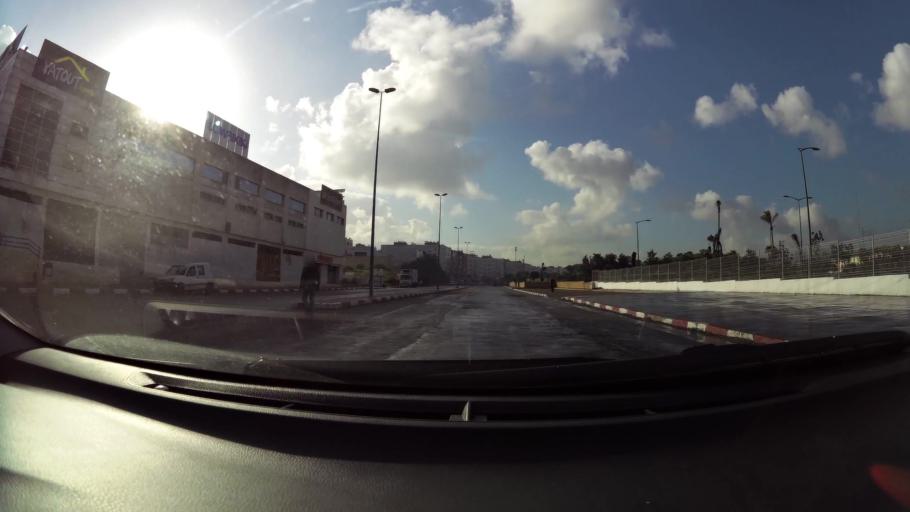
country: MA
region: Grand Casablanca
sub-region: Mediouna
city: Tit Mellil
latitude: 33.6017
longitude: -7.5274
